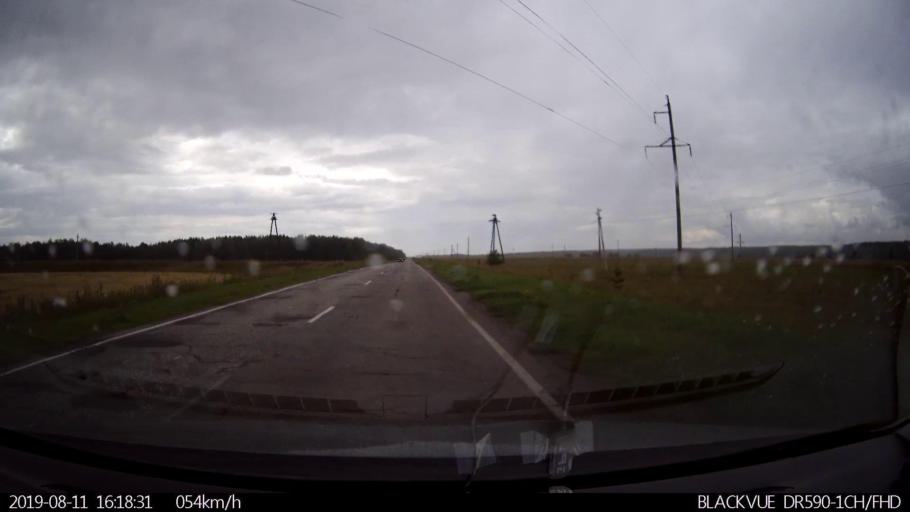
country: RU
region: Ulyanovsk
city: Mayna
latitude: 54.0564
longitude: 47.6112
